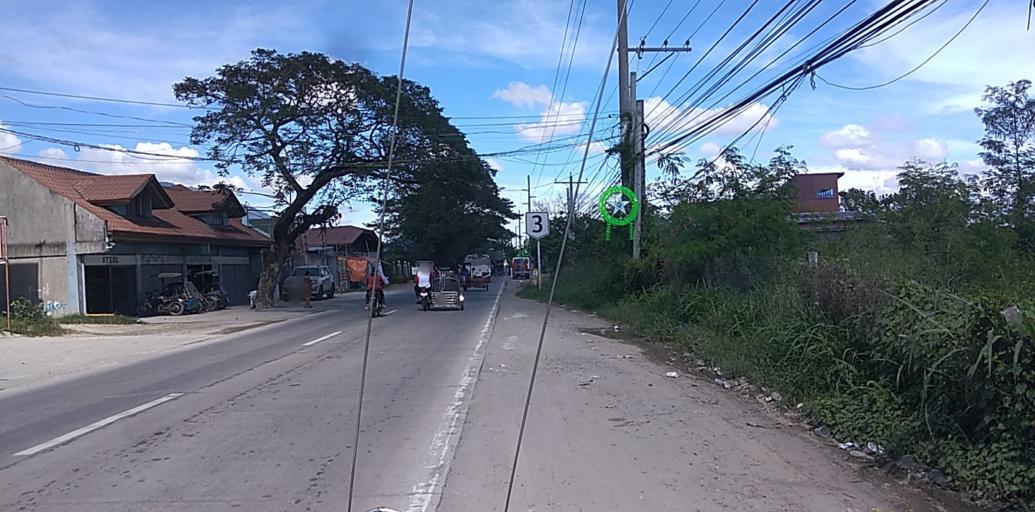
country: PH
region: Central Luzon
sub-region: Province of Pampanga
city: Santa Ana
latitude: 15.1216
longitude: 120.7758
